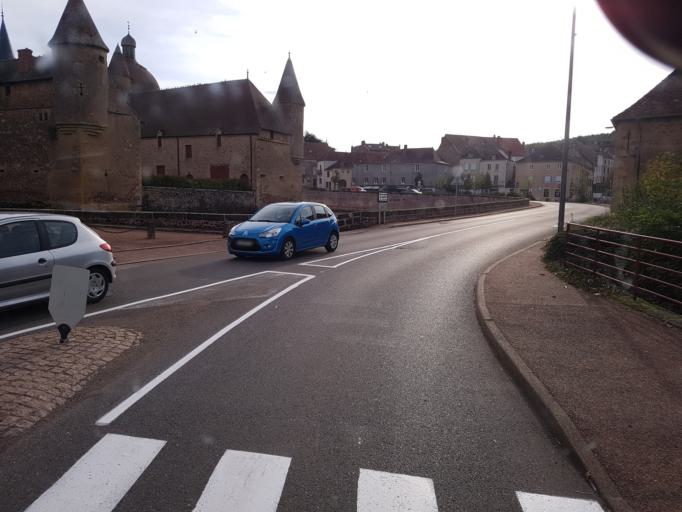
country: FR
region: Bourgogne
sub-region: Departement de Saone-et-Loire
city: La Clayette
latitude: 46.2931
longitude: 4.3048
